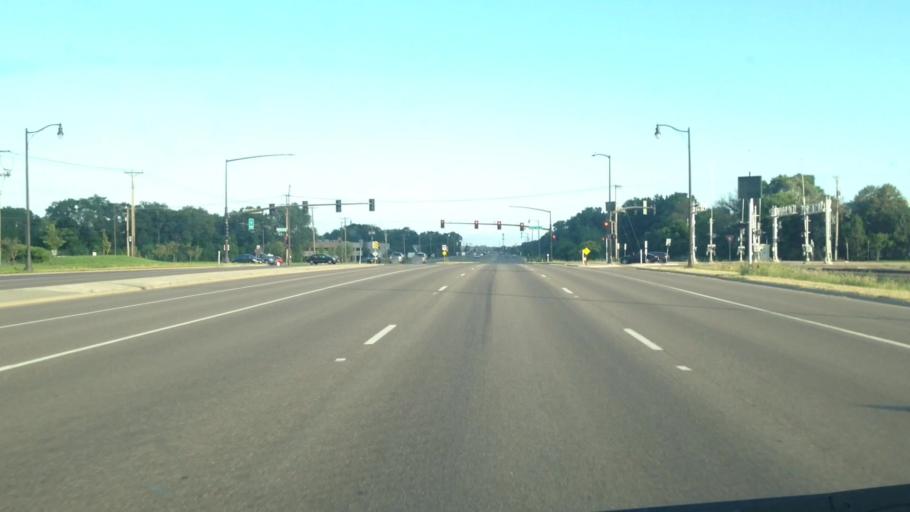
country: US
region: Minnesota
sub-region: Hennepin County
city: Brooklyn Park
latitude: 45.0703
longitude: -93.3687
